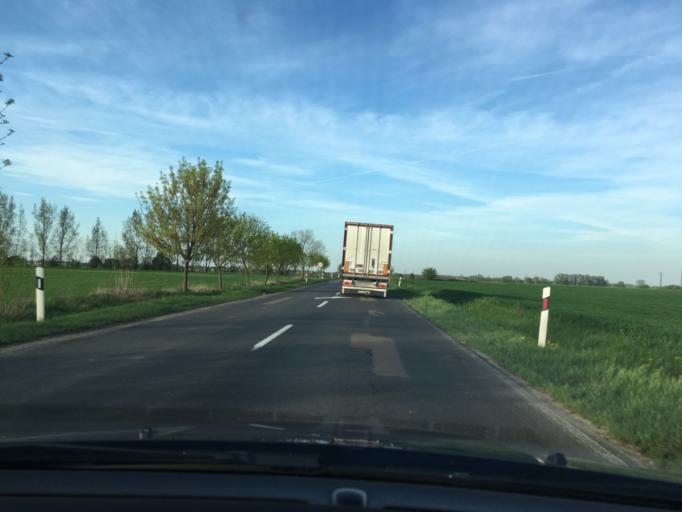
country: HU
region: Hajdu-Bihar
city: Berettyoujfalu
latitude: 47.1807
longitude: 21.5282
